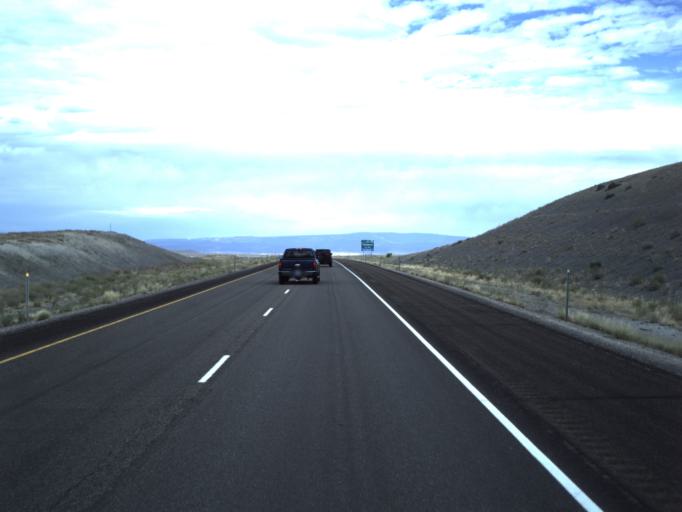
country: US
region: Utah
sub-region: Grand County
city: Moab
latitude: 38.9423
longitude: -109.6323
